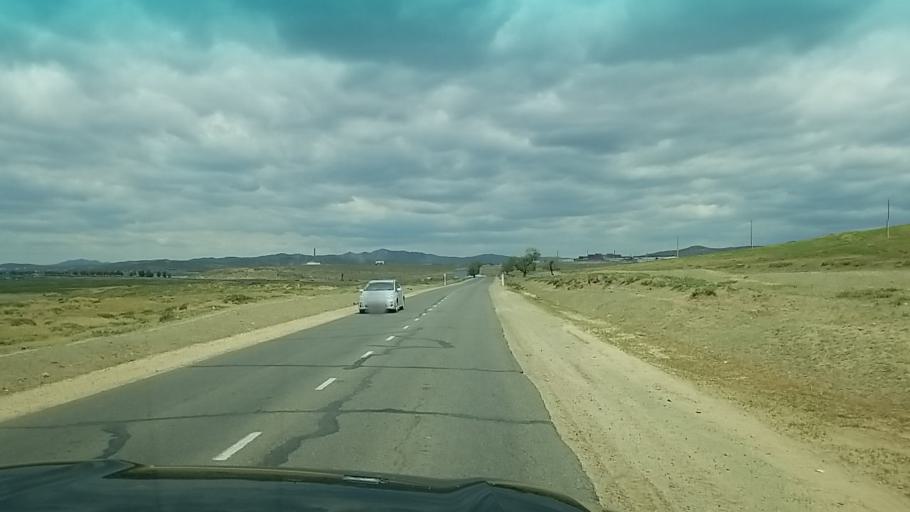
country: MN
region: Darhan Uul
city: Darhan
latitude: 49.4057
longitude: 105.9368
